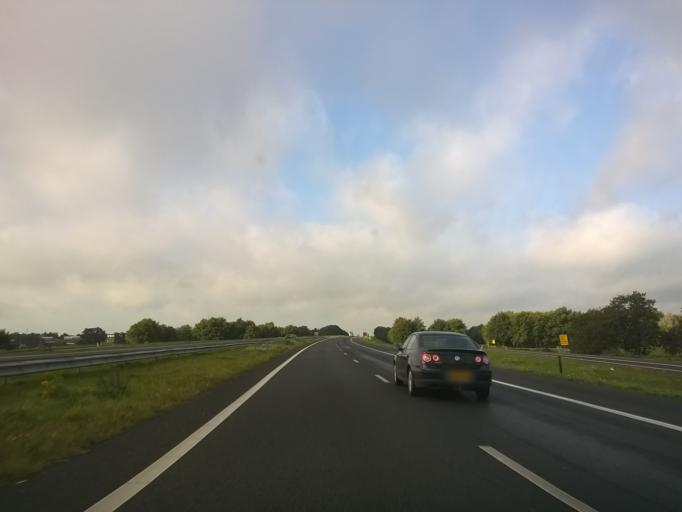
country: NL
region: Groningen
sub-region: Gemeente Grootegast
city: Grootegast
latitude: 53.1559
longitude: 6.2767
